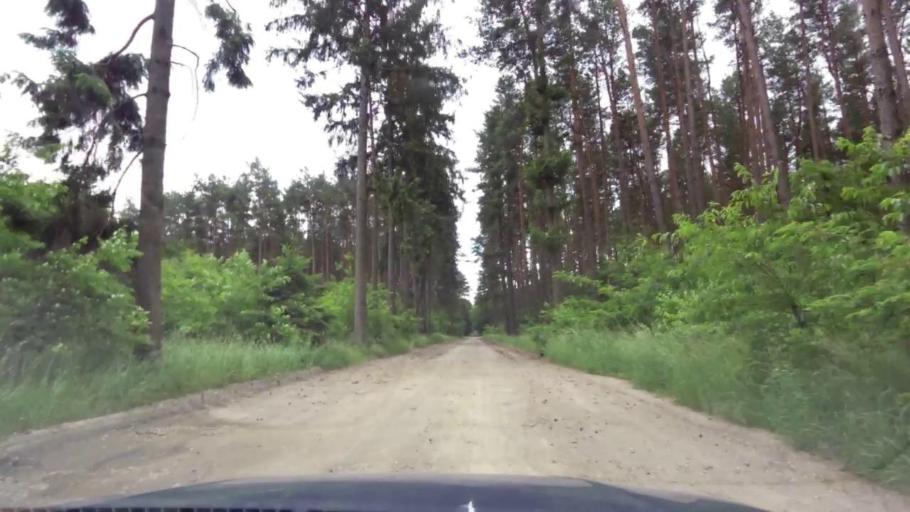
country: PL
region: West Pomeranian Voivodeship
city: Trzcinsko Zdroj
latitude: 52.8678
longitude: 14.5846
